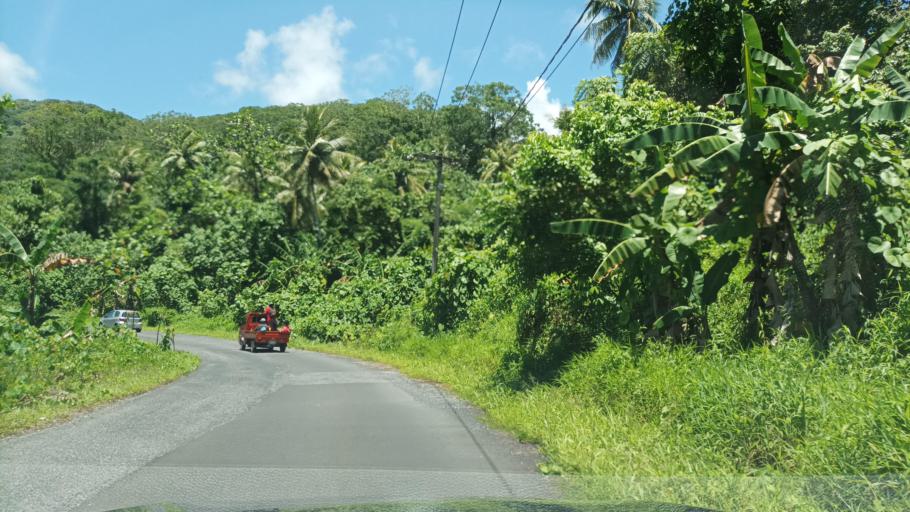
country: FM
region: Pohnpei
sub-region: Madolenihm Municipality
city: Madolenihm Municipality Government
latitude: 6.9174
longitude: 158.3211
